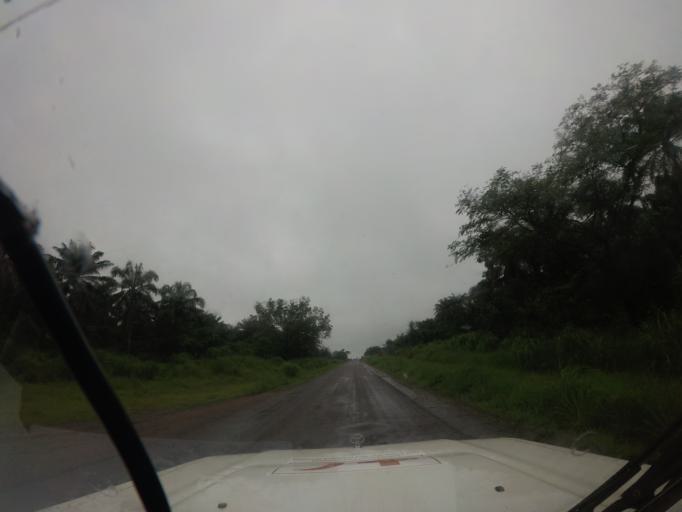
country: SL
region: Northern Province
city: Binkolo
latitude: 8.9419
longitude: -11.9889
